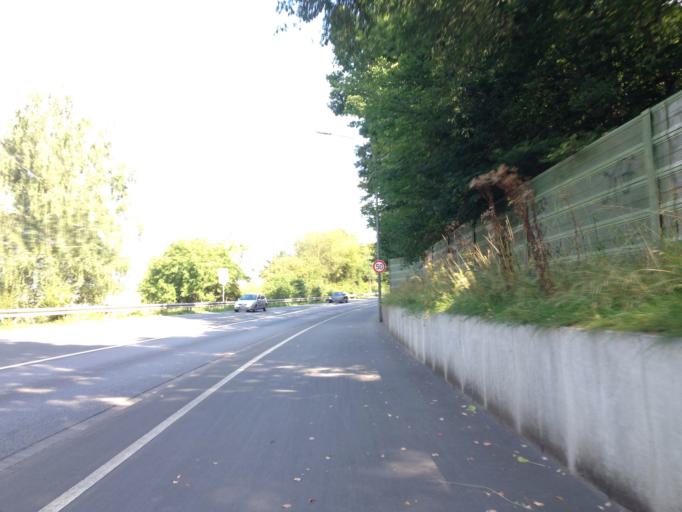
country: DE
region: Hesse
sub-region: Regierungsbezirk Giessen
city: Giessen
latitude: 50.5944
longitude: 8.7050
